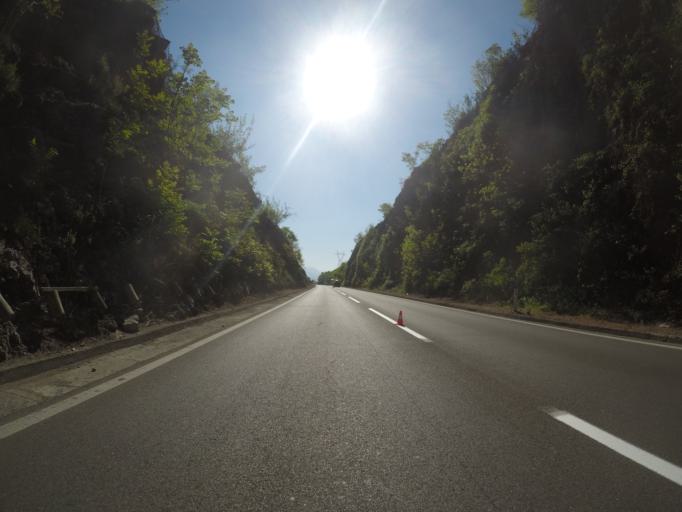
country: ME
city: Spuz
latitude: 42.4565
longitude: 19.1837
